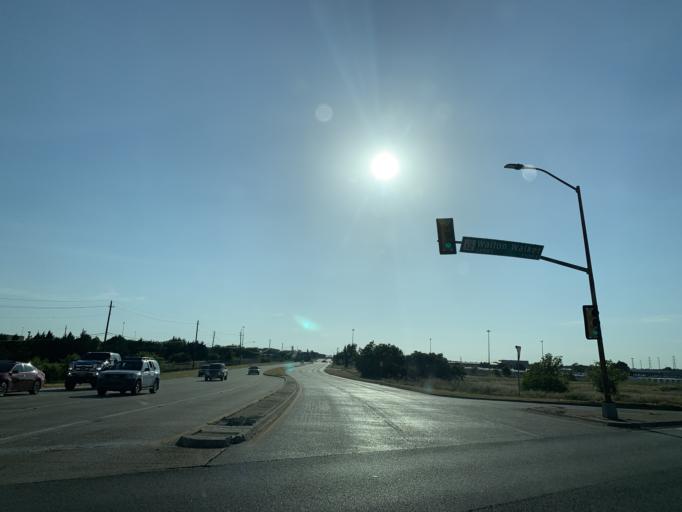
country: US
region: Texas
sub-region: Dallas County
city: Cockrell Hill
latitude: 32.7058
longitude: -96.9038
